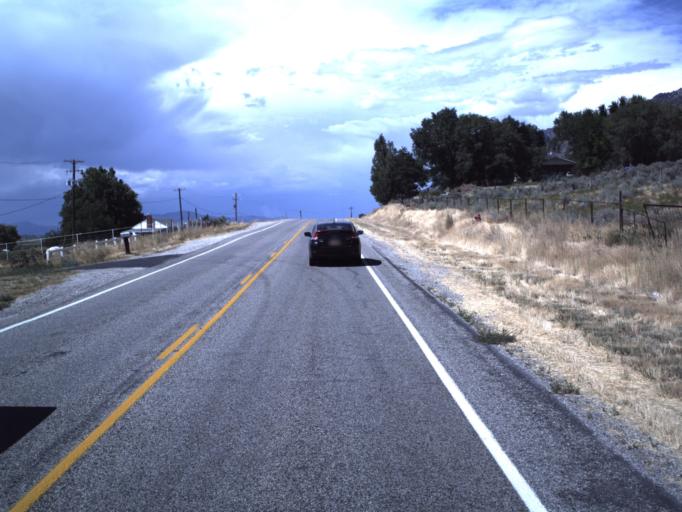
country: US
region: Utah
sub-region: Box Elder County
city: Brigham City
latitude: 41.5502
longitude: -112.0182
